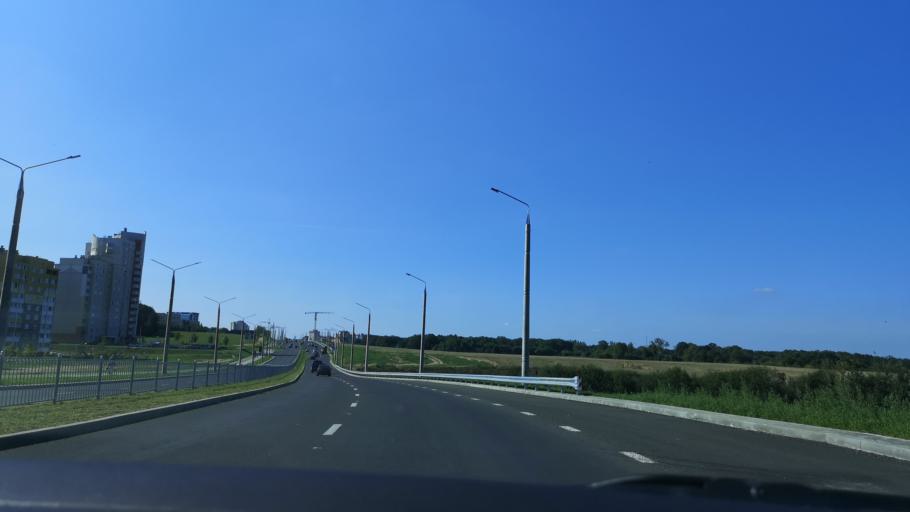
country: BY
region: Grodnenskaya
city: Hrodna
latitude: 53.6453
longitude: 23.8713
